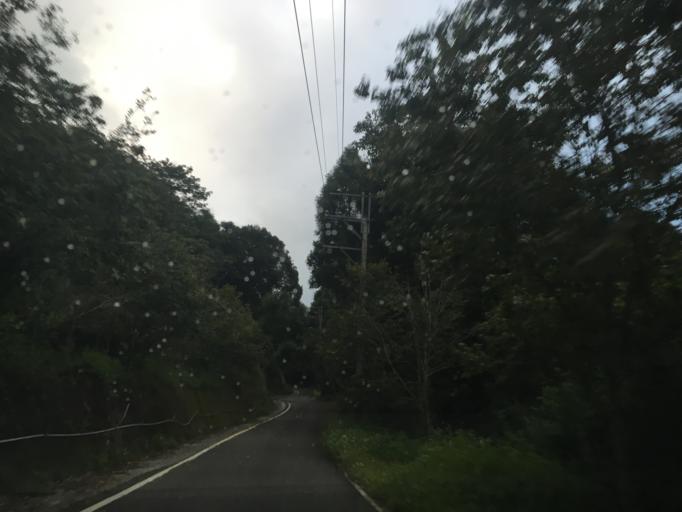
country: TW
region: Taiwan
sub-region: Nantou
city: Puli
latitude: 23.9032
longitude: 120.9101
